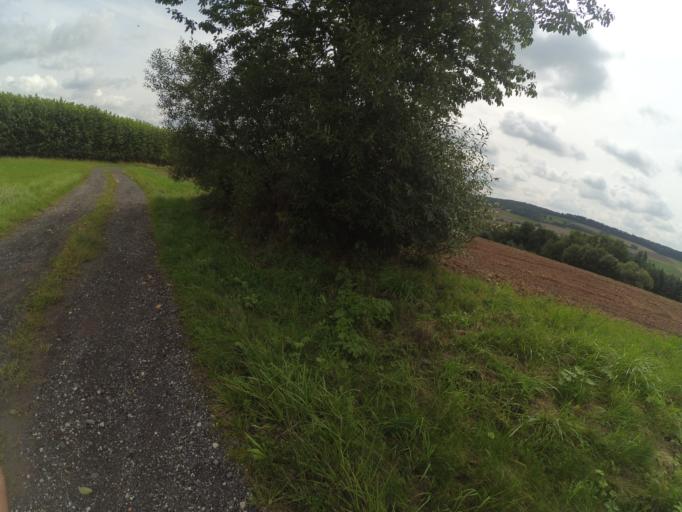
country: DE
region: Hesse
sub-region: Regierungsbezirk Kassel
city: Kirchheim
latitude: 50.8575
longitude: 9.5407
